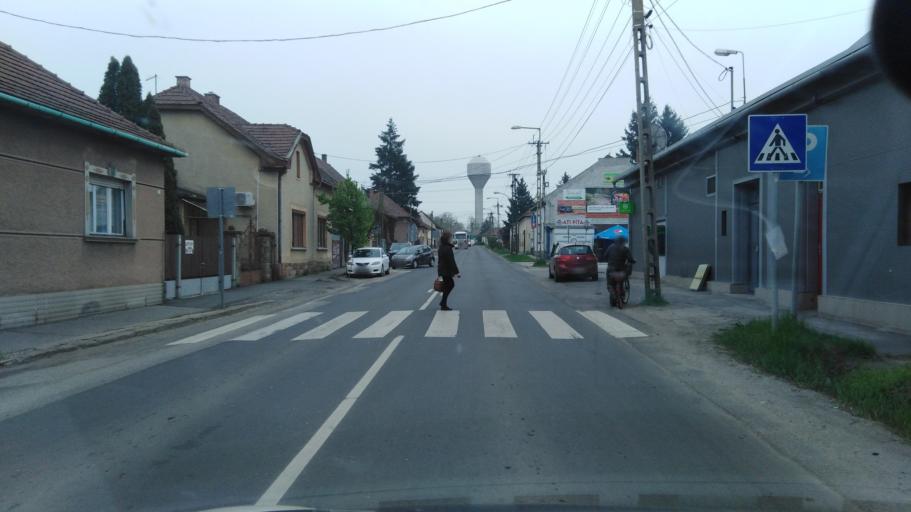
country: HU
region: Nograd
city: Balassagyarmat
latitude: 48.0714
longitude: 19.2965
